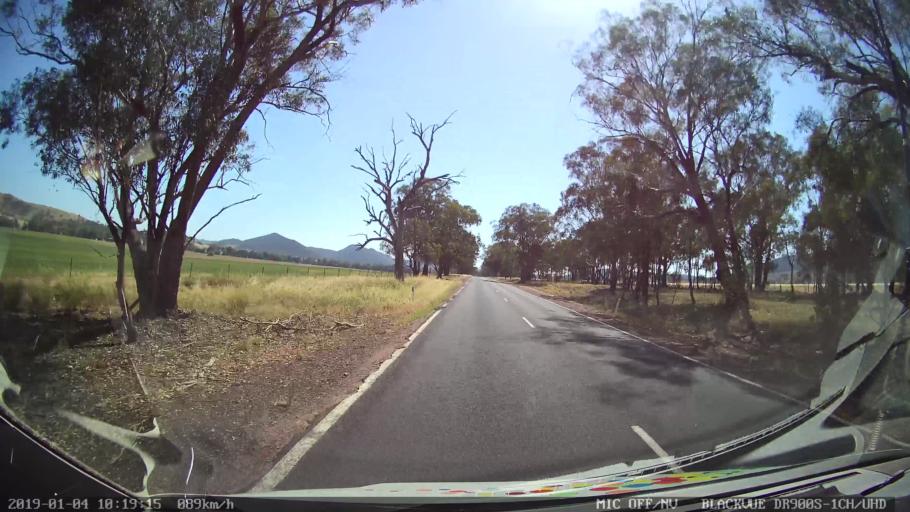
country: AU
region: New South Wales
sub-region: Cabonne
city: Canowindra
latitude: -33.3776
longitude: 148.4779
